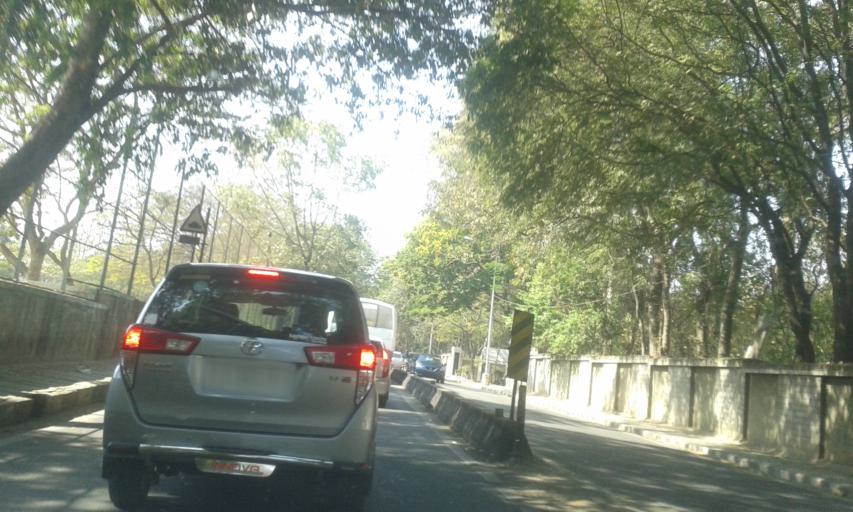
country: IN
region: Karnataka
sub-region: Bangalore Urban
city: Bangalore
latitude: 13.0104
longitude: 77.5704
